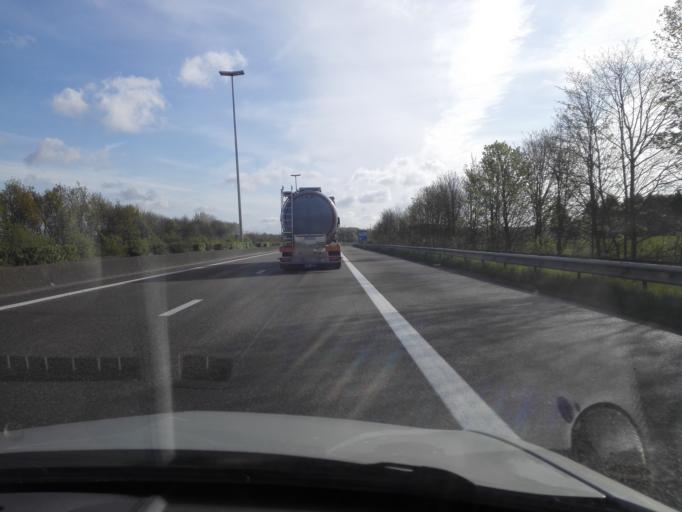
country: BE
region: Flanders
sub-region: Provincie Vlaams-Brabant
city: Aarschot
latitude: 50.9589
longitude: 4.8117
